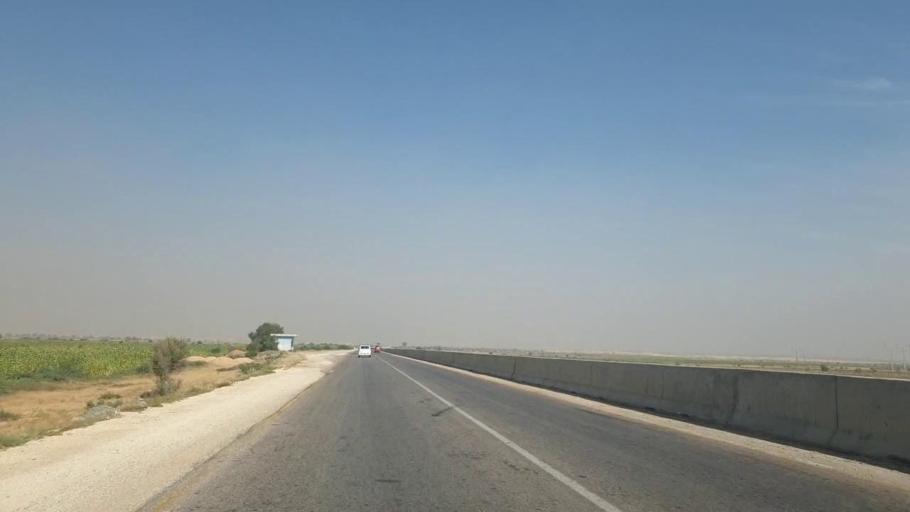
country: PK
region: Sindh
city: Jamshoro
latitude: 25.5377
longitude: 68.2865
